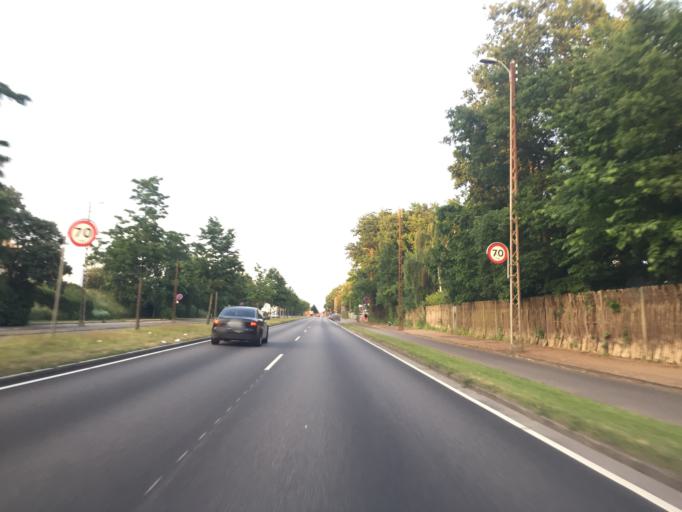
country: DK
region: Capital Region
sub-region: Rodovre Kommune
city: Rodovre
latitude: 55.6696
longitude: 12.4400
